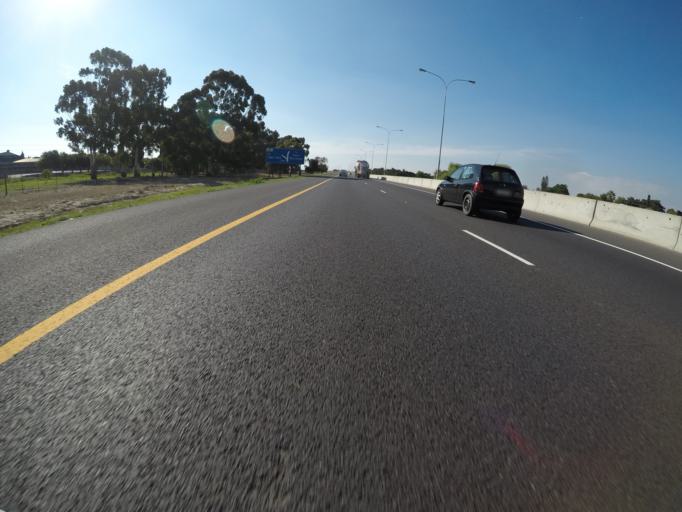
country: ZA
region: Western Cape
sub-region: City of Cape Town
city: Kraaifontein
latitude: -33.8853
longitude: 18.6749
